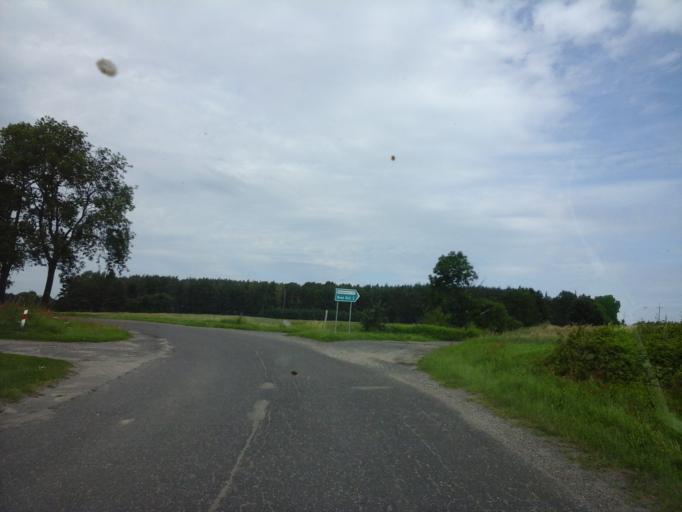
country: PL
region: Lubusz
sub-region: Powiat strzelecko-drezdenecki
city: Dobiegniew
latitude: 53.0198
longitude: 15.7432
